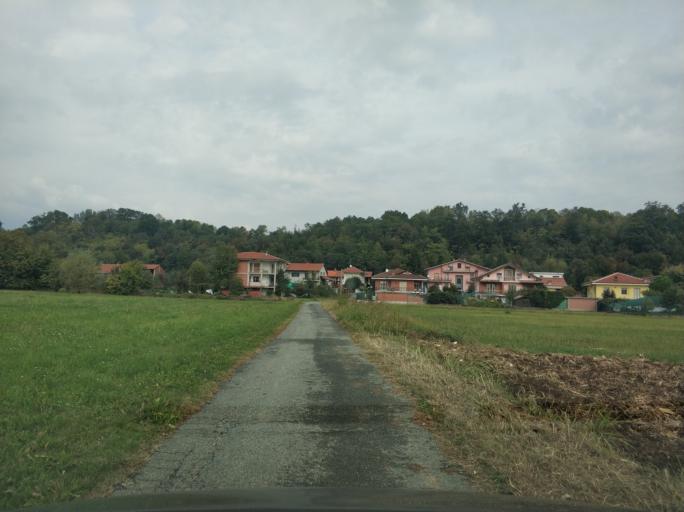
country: IT
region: Piedmont
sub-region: Provincia di Torino
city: Nole
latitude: 45.2555
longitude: 7.5731
